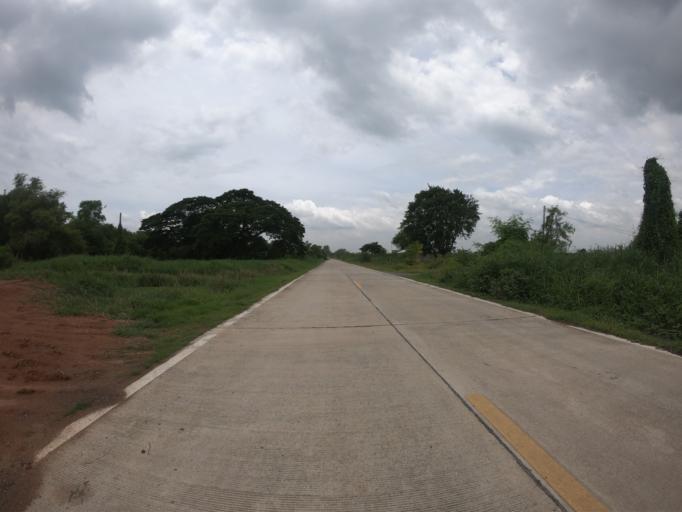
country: TH
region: Pathum Thani
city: Ban Lam Luk Ka
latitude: 13.9652
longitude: 100.8527
